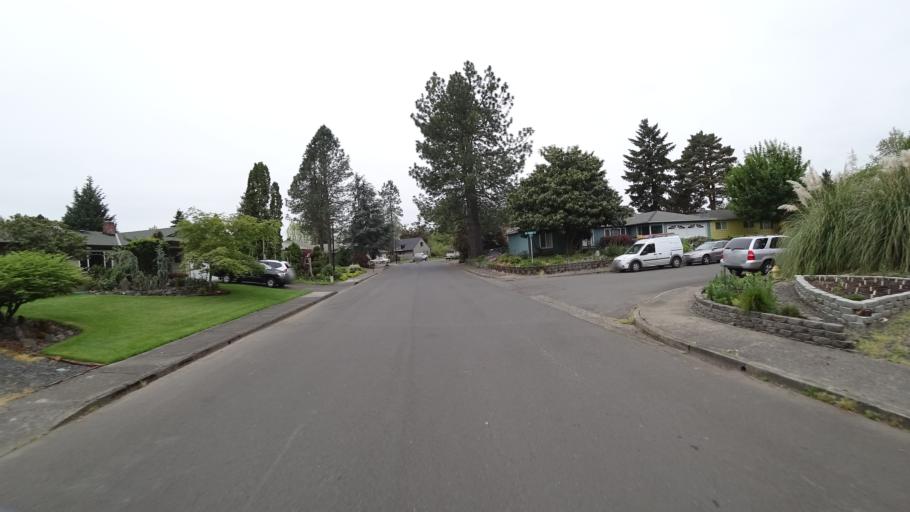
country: US
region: Oregon
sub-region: Washington County
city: Aloha
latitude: 45.5045
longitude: -122.8832
